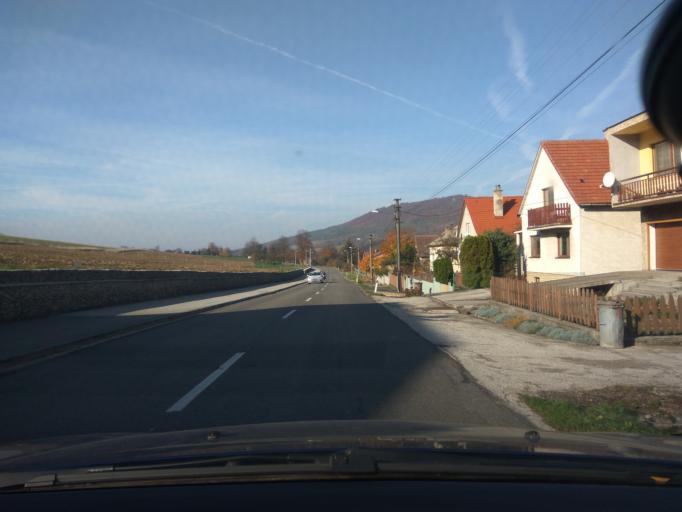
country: SK
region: Nitriansky
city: Brezova pod Bradlom
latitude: 48.6713
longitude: 17.5935
